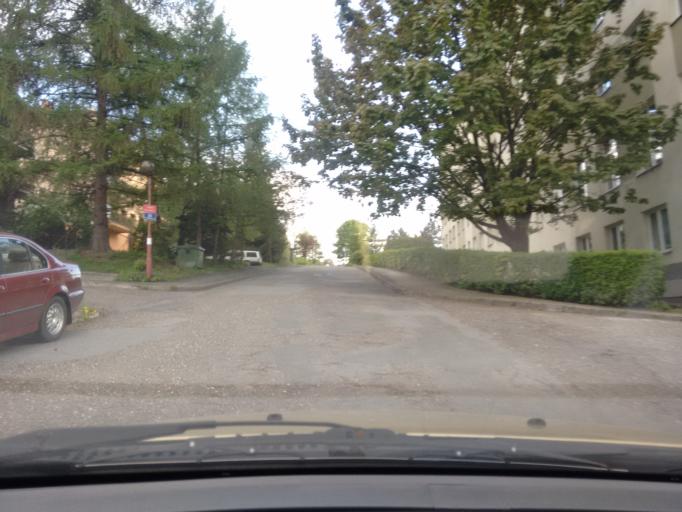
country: PL
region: Silesian Voivodeship
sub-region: Powiat cieszynski
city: Cieszyn
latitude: 49.7481
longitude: 18.6496
